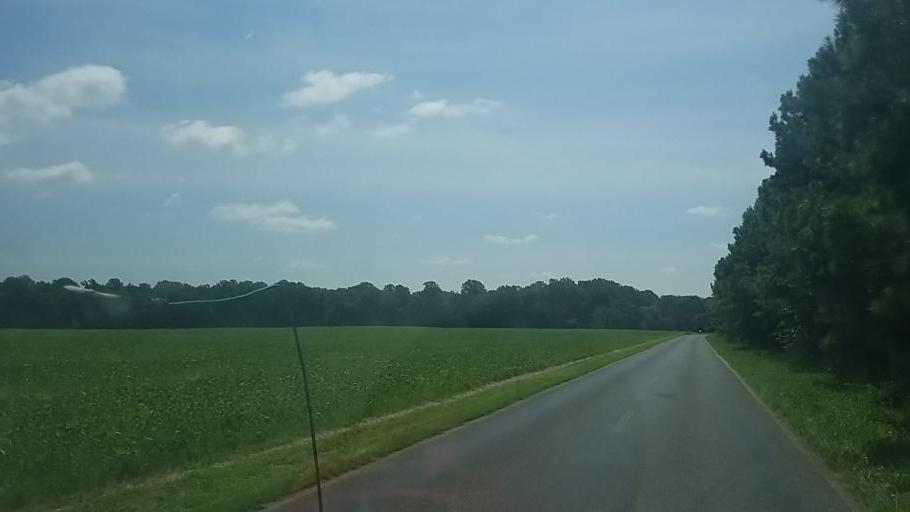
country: US
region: Maryland
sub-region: Caroline County
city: Ridgely
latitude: 38.8880
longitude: -75.9272
